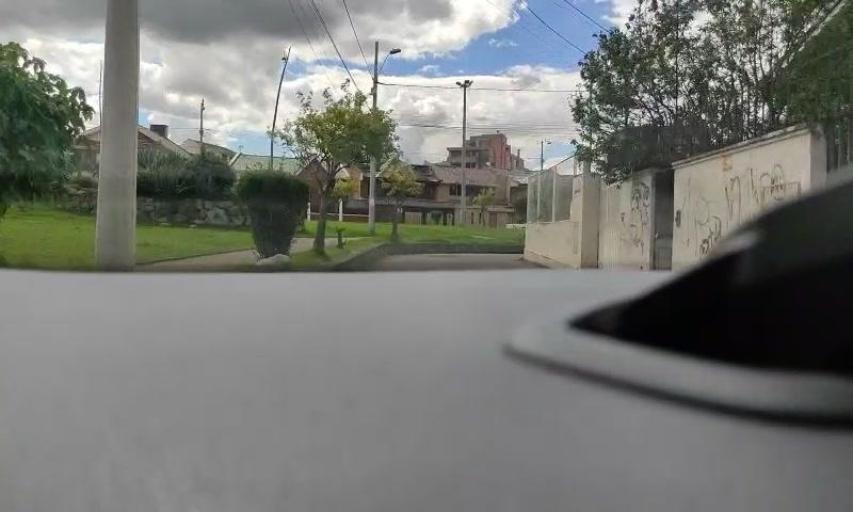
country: EC
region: Azuay
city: Cuenca
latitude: -2.9119
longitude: -79.0195
